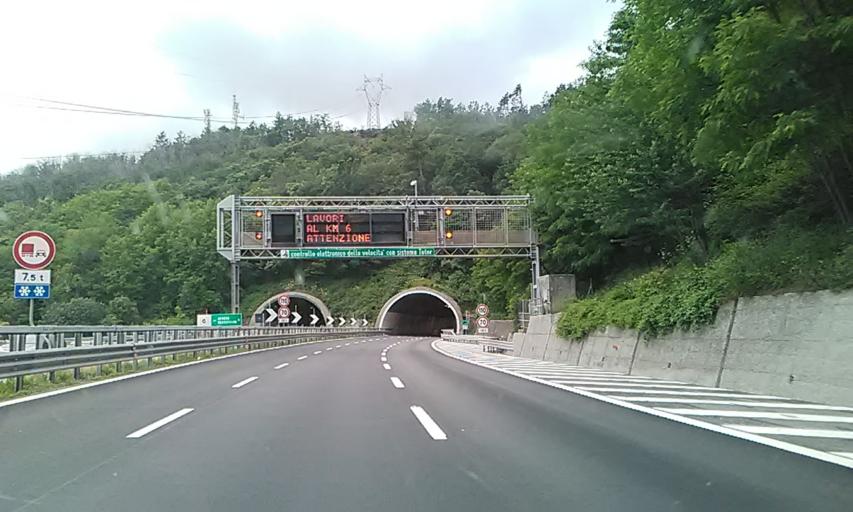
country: IT
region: Liguria
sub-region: Provincia di Genova
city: Mele
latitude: 44.4488
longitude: 8.7384
